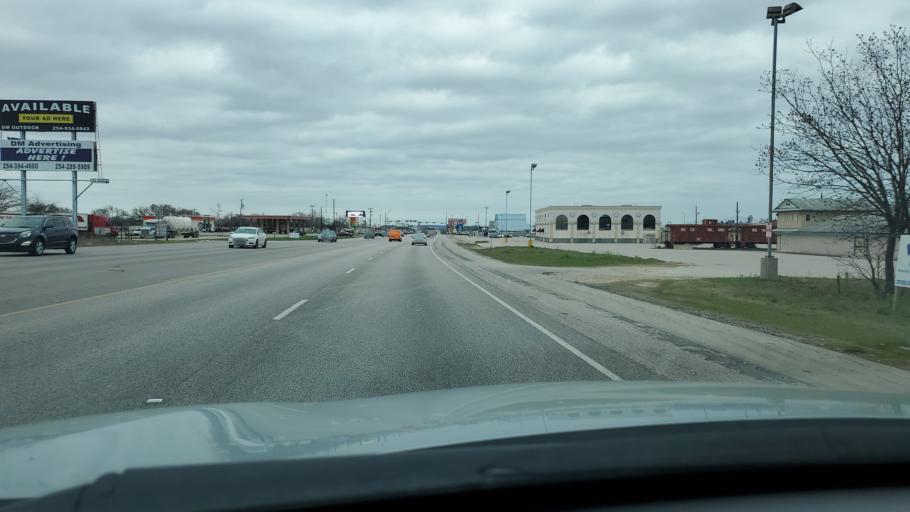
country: US
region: Texas
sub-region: Bell County
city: Killeen
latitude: 31.0835
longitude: -97.7564
